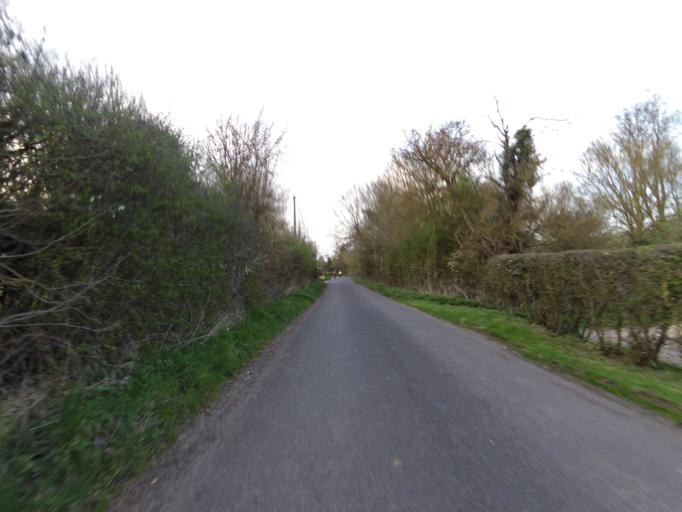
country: GB
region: England
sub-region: Suffolk
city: Debenham
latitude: 52.1501
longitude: 1.2063
